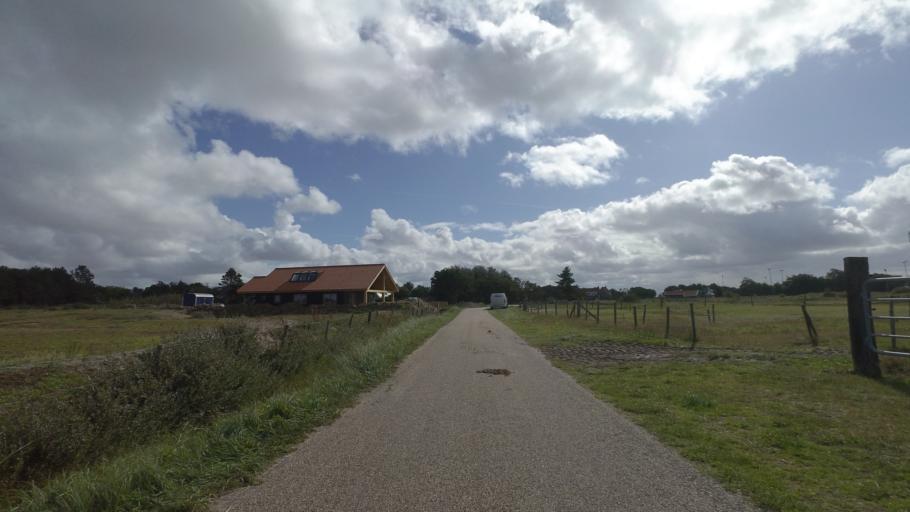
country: NL
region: Friesland
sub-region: Gemeente Ameland
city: Nes
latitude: 53.4502
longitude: 5.7933
